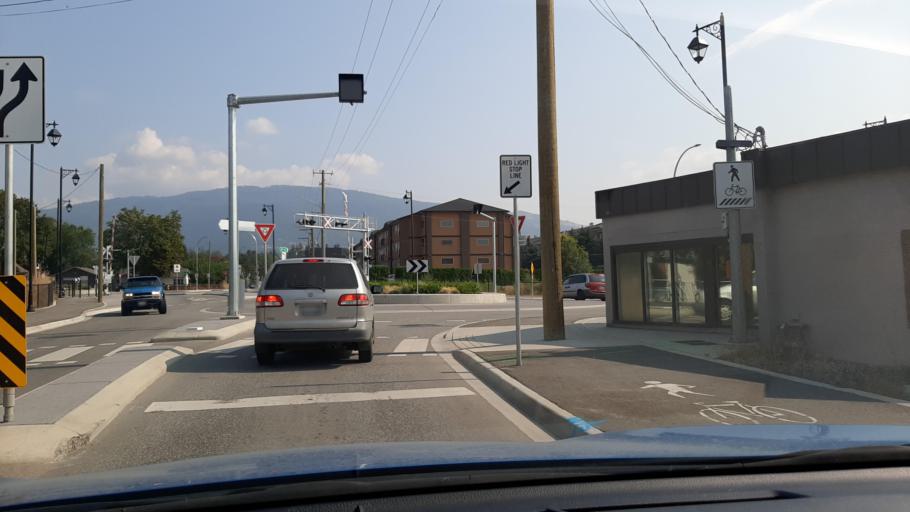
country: CA
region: British Columbia
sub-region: Regional District of North Okanagan
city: Vernon
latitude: 50.2701
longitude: -119.2711
